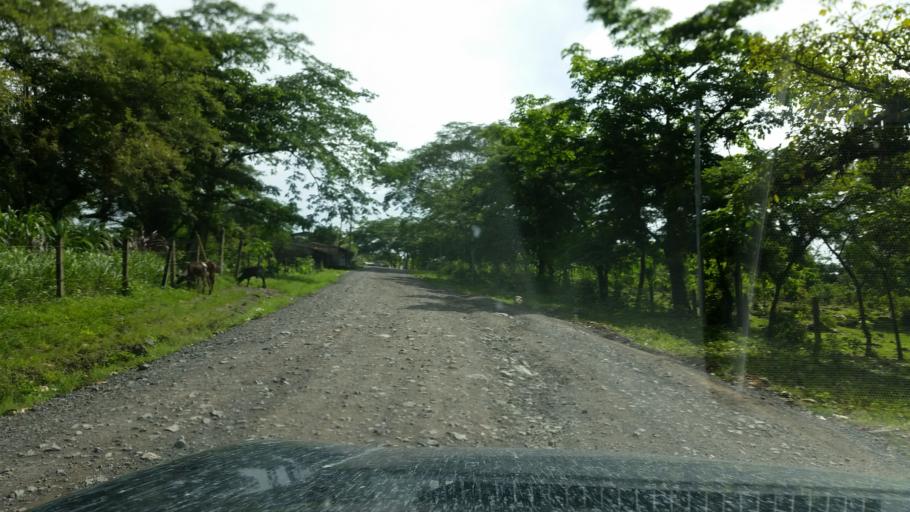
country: NI
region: Atlantico Norte (RAAN)
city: Siuna
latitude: 13.7187
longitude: -84.7652
